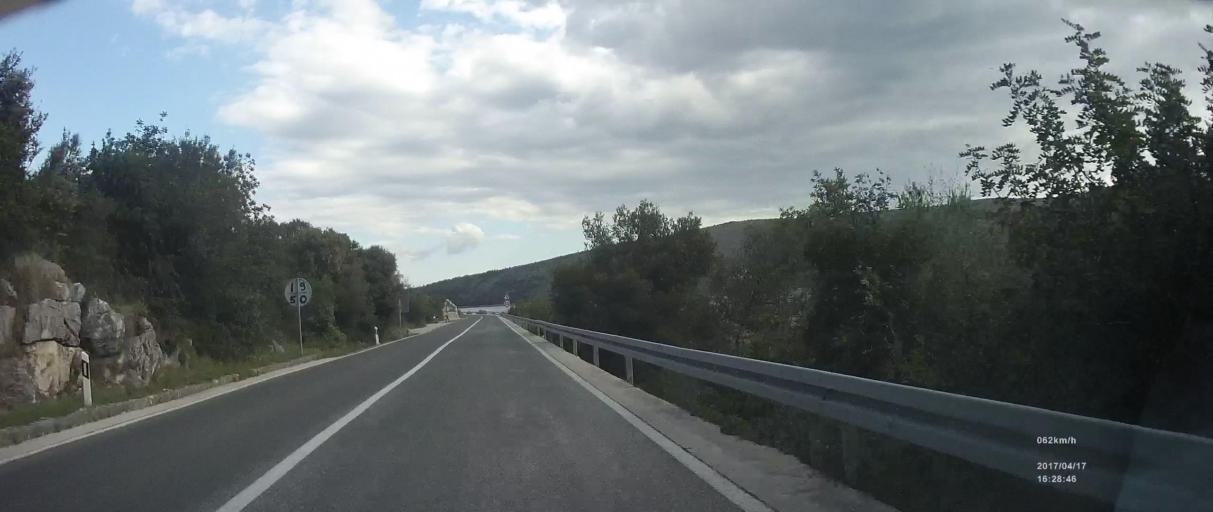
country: HR
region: Splitsko-Dalmatinska
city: Veliki Drvenik
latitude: 43.5150
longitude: 16.1575
